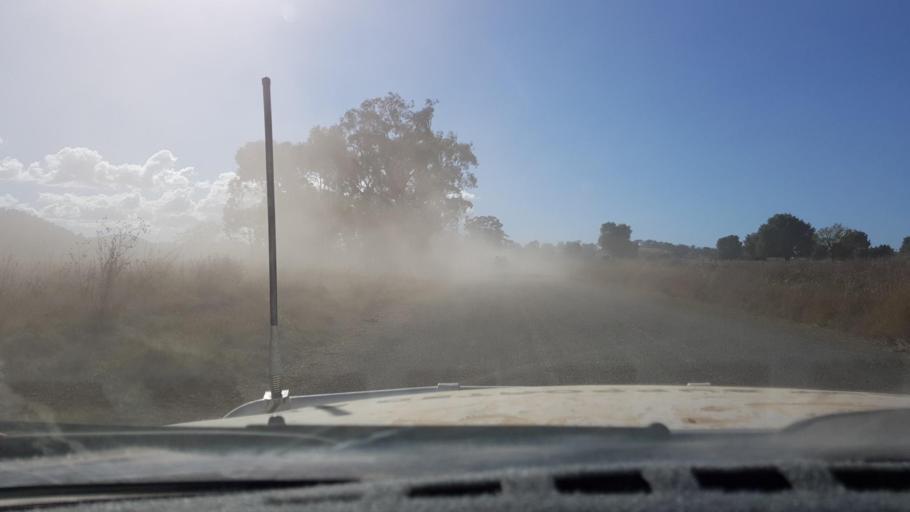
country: AU
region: New South Wales
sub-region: Narrabri
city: Blair Athol
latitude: -30.6693
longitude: 150.4574
